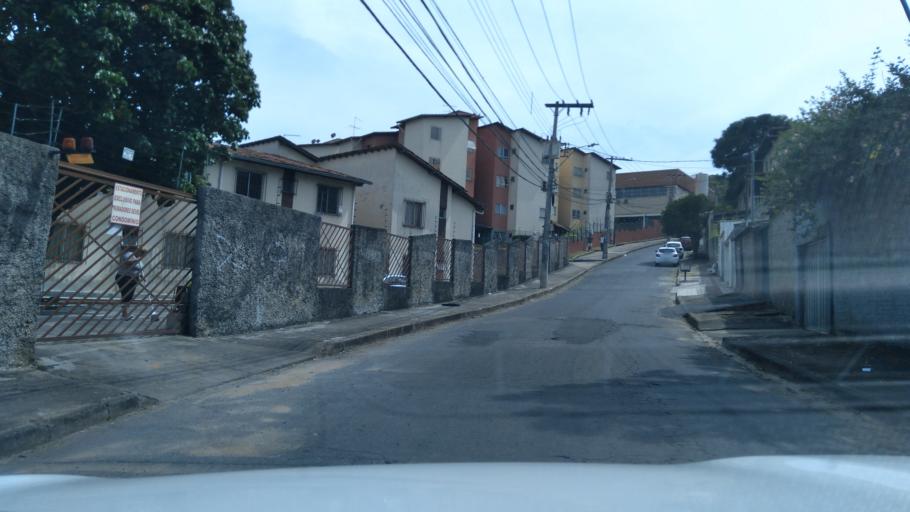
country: BR
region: Minas Gerais
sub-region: Contagem
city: Contagem
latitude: -19.8973
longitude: -44.0096
